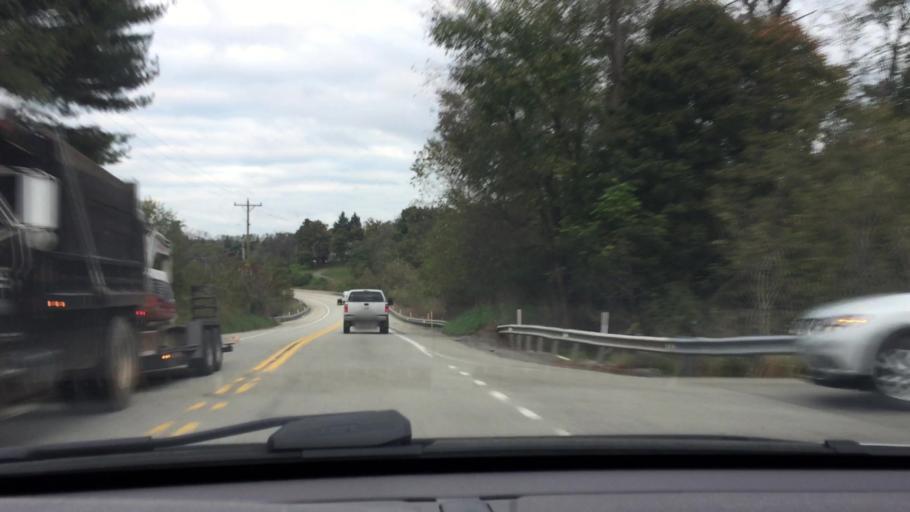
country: US
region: Pennsylvania
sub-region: Washington County
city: Canonsburg
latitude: 40.2157
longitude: -80.1369
